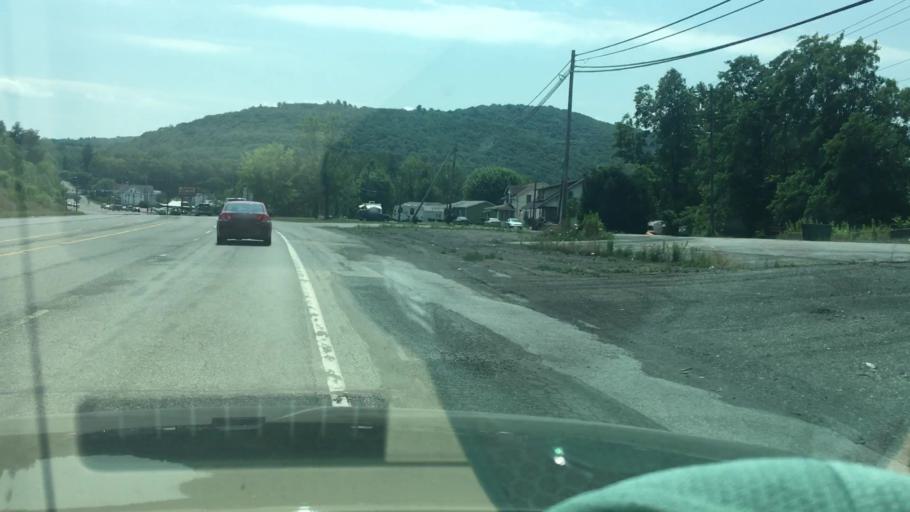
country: US
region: Pennsylvania
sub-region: Schuylkill County
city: Tamaqua
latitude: 40.7604
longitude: -75.9484
